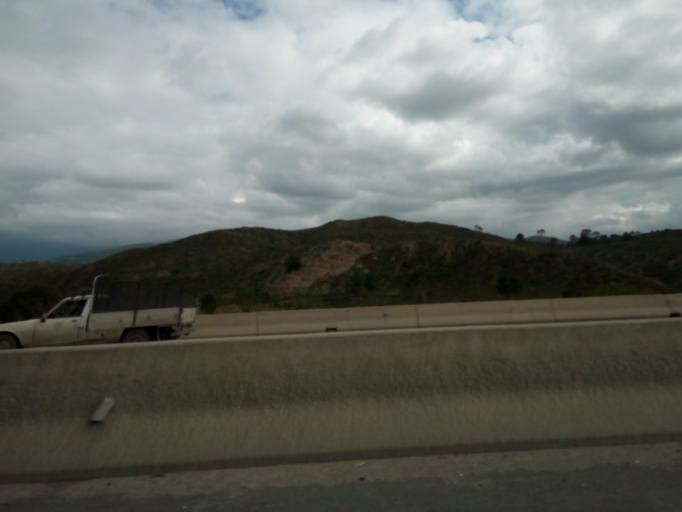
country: DZ
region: Bordj Bou Arreridj
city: Mansourah
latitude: 36.1954
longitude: 4.4388
